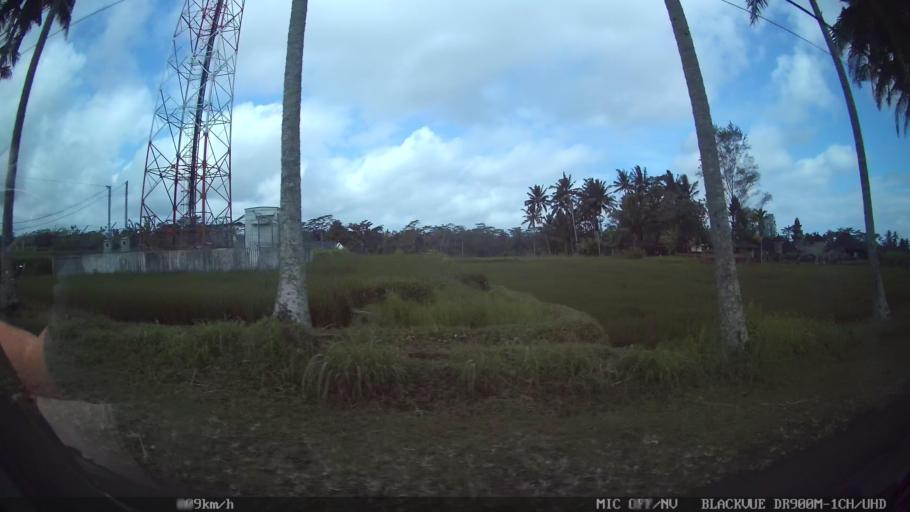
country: ID
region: Bali
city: Banjar Pesalakan
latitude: -8.4997
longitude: 115.3044
